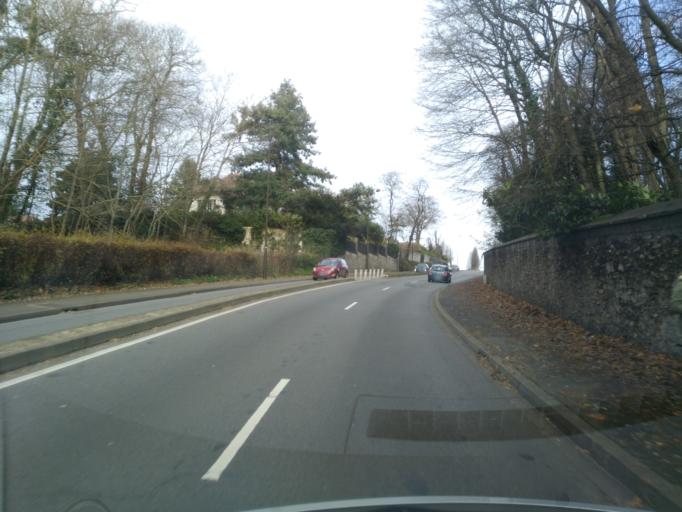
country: FR
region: Ile-de-France
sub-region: Departement des Yvelines
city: Le Chesnay
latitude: 48.8324
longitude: 2.1284
